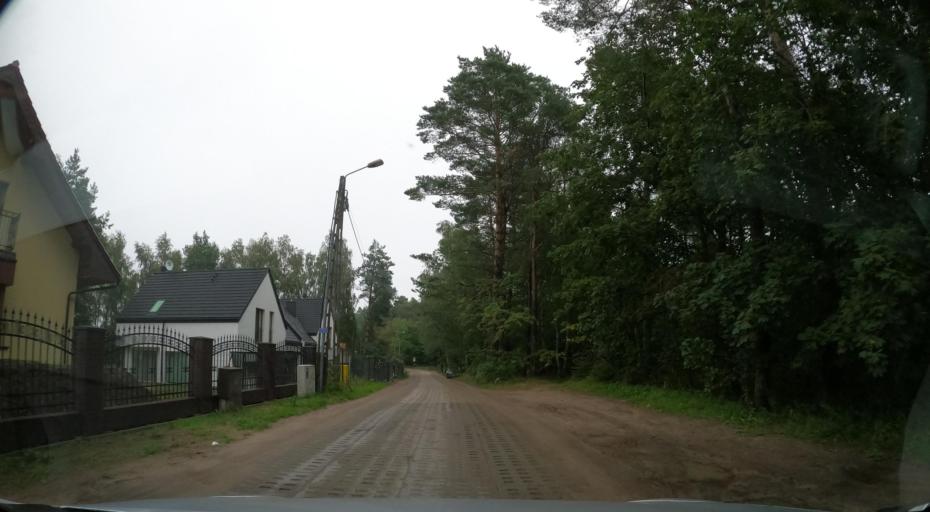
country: PL
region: Pomeranian Voivodeship
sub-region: Powiat kartuski
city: Chwaszczyno
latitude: 54.4169
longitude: 18.4355
